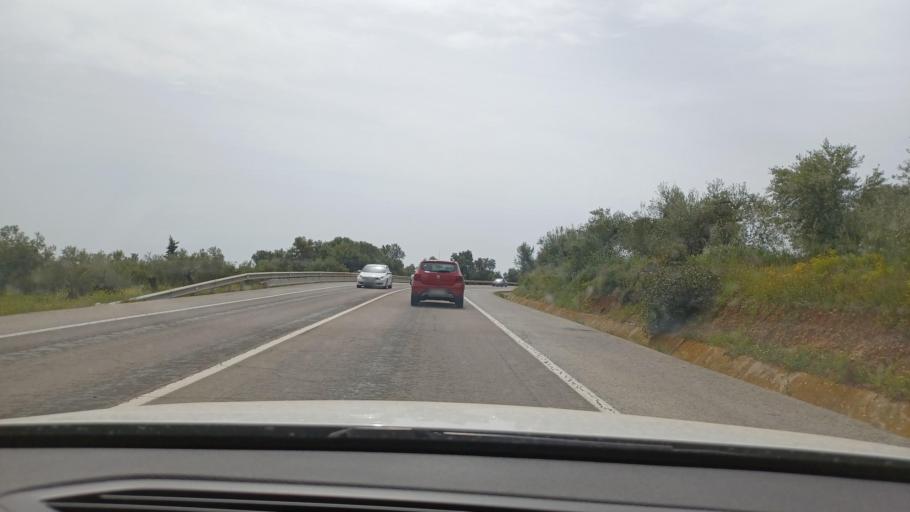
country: ES
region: Catalonia
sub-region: Provincia de Tarragona
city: Sant Carles de la Rapita
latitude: 40.6593
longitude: 0.5869
